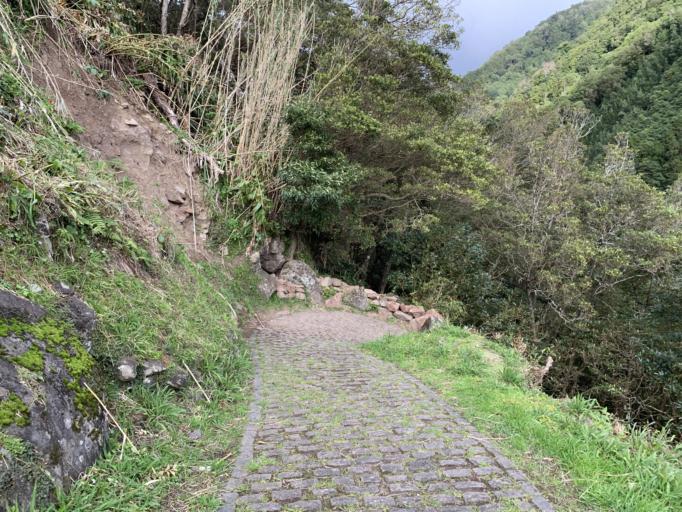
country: PT
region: Azores
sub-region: Povoacao
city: Furnas
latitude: 37.7509
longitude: -25.2028
